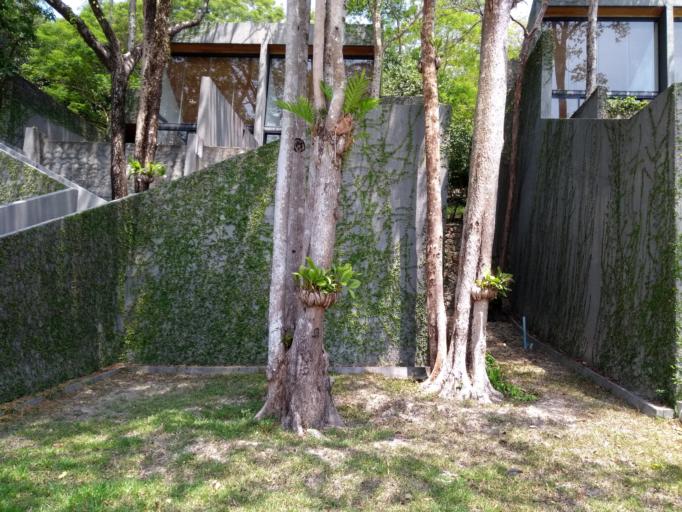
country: TH
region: Trat
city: Ko Chang Tai
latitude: 11.8332
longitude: 102.4604
